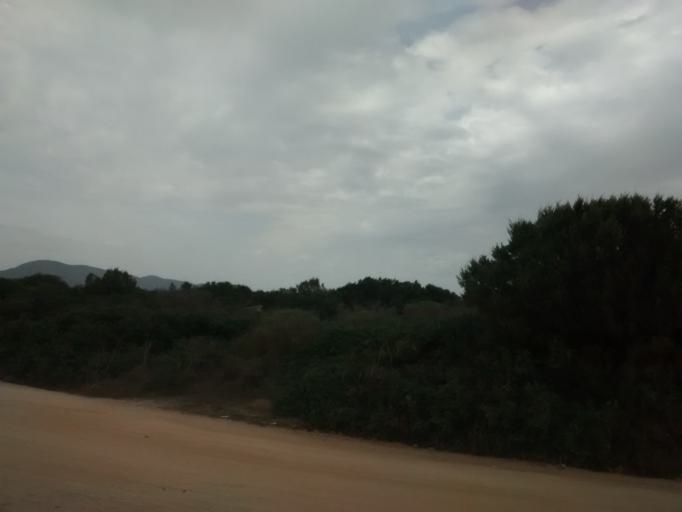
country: IT
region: Sardinia
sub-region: Provincia di Cagliari
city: Villasimius
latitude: 39.1079
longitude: 9.5151
